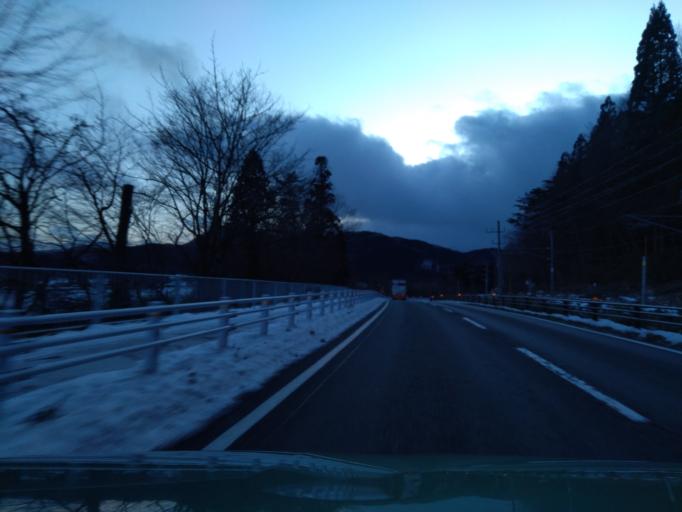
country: JP
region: Iwate
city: Shizukuishi
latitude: 39.6902
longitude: 140.9237
